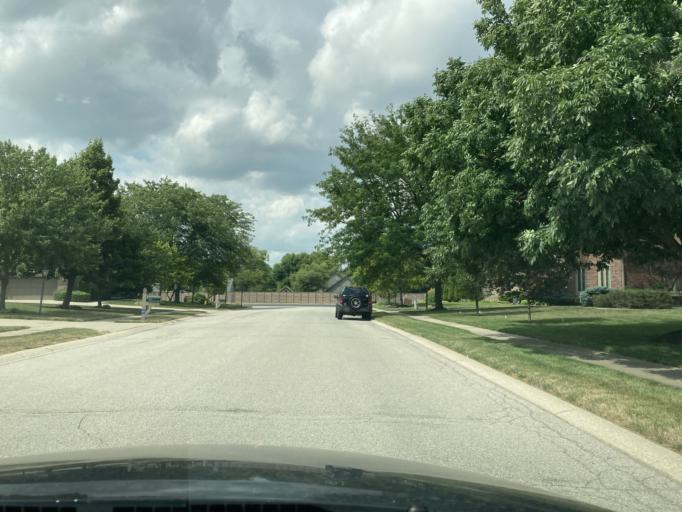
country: US
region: Indiana
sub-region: Hamilton County
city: Carmel
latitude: 39.9987
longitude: -86.1559
